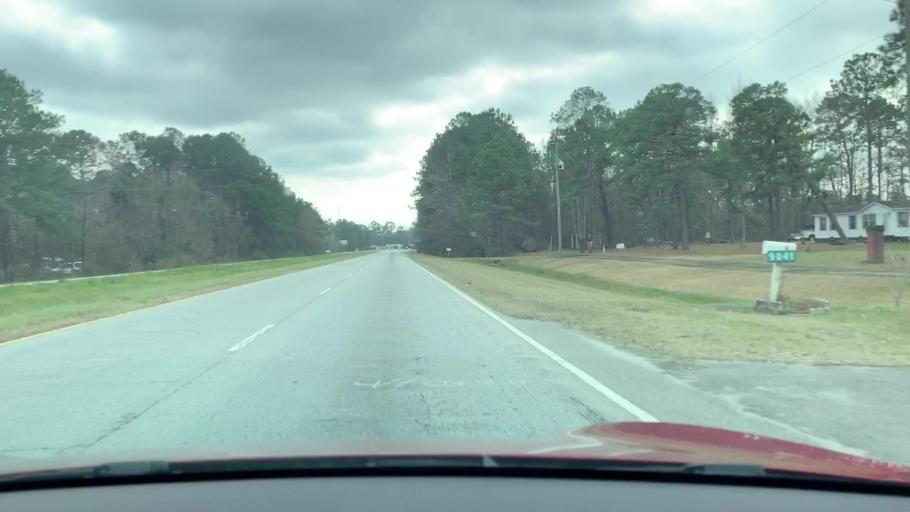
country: US
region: South Carolina
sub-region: Jasper County
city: Hardeeville
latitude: 32.2152
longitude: -81.0726
